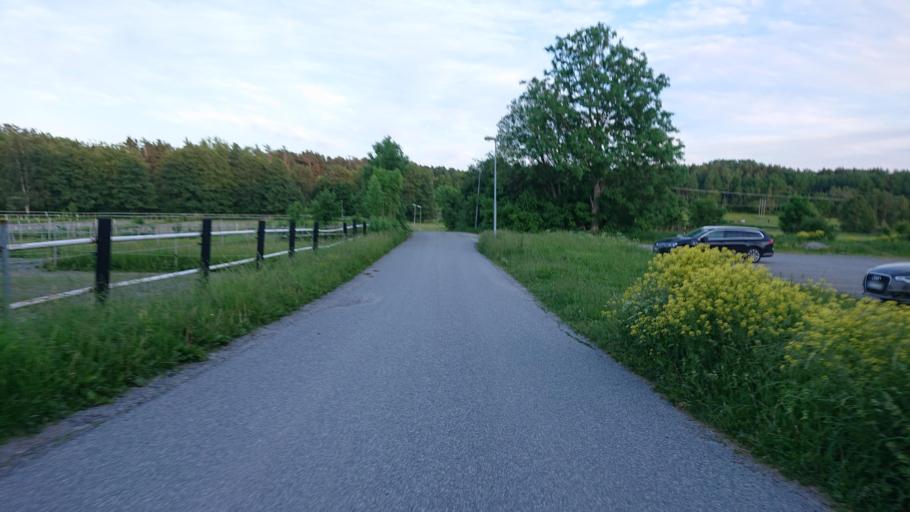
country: SE
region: Stockholm
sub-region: Osterakers Kommun
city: Akersberga
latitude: 59.5024
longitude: 18.3100
